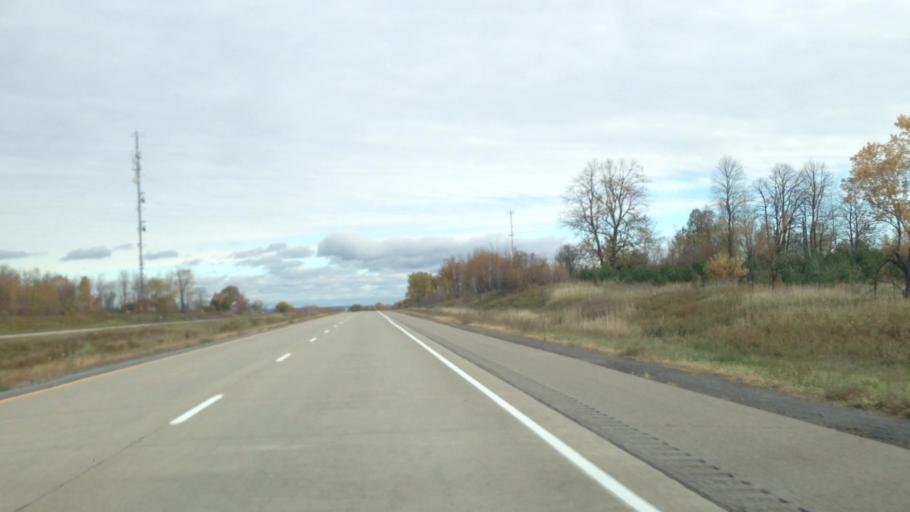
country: CA
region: Ontario
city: Hawkesbury
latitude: 45.5572
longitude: -74.5156
